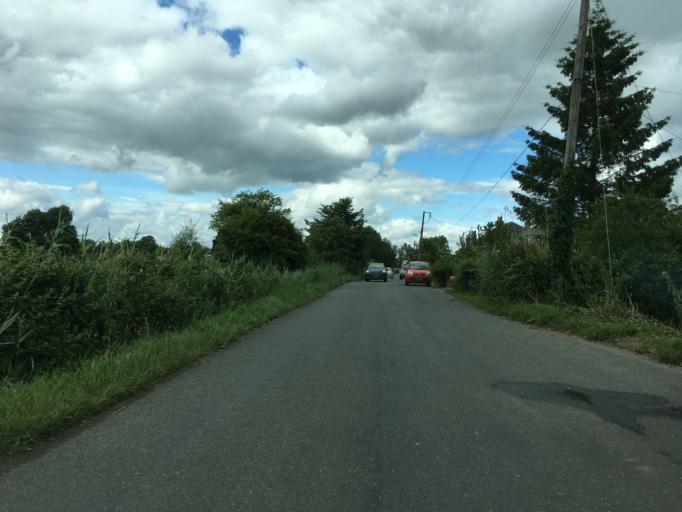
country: GB
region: England
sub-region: Gloucestershire
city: Stonehouse
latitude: 51.7868
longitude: -2.3643
